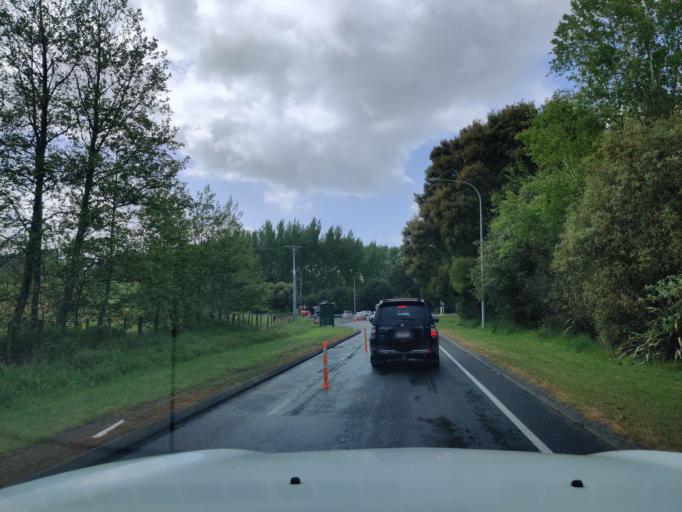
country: NZ
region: Waikato
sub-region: Hamilton City
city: Hamilton
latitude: -37.8273
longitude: 175.3569
